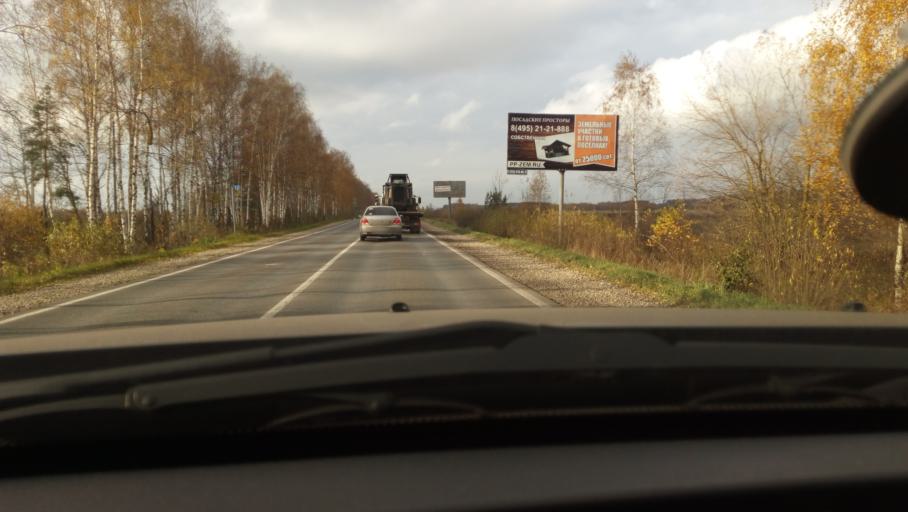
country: RU
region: Moskovskaya
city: Rakhmanovo
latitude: 55.7515
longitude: 38.6303
